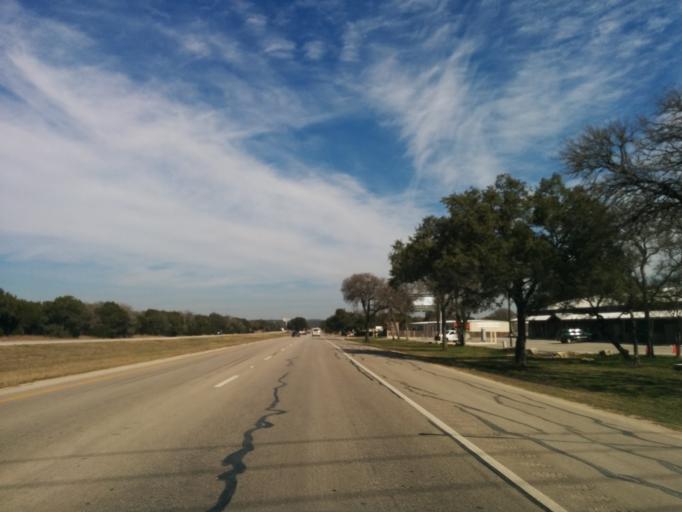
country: US
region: Texas
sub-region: Comal County
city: Bulverde
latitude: 29.8403
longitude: -98.4102
